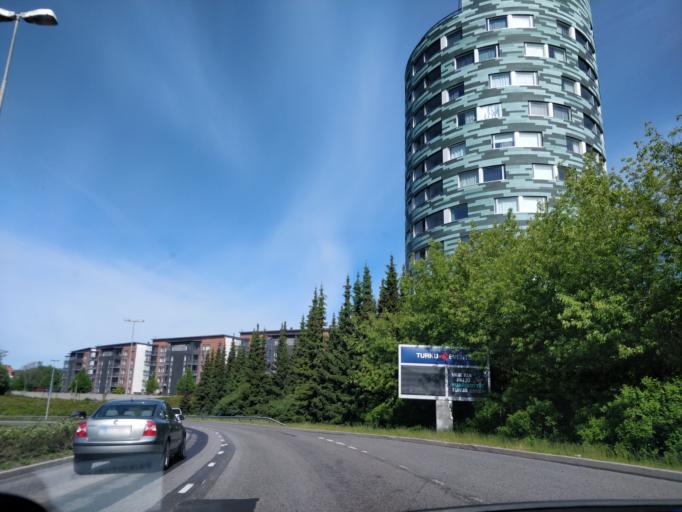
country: FI
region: Varsinais-Suomi
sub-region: Turku
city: Turku
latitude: 60.4602
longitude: 22.2866
